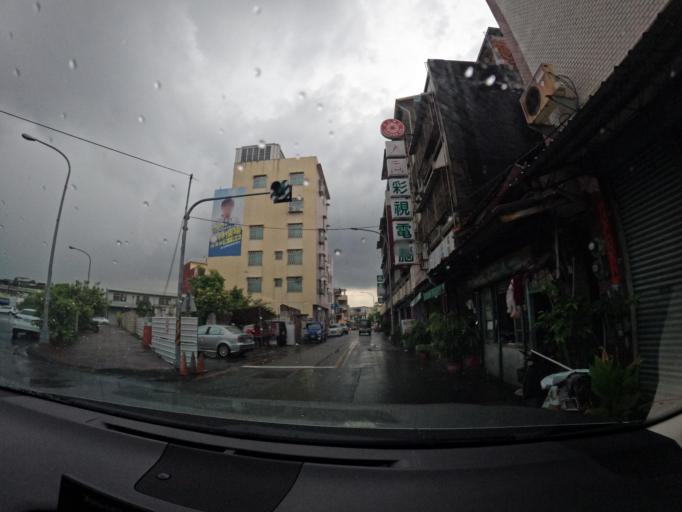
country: TW
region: Taiwan
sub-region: Nantou
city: Nantou
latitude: 23.9089
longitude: 120.6904
